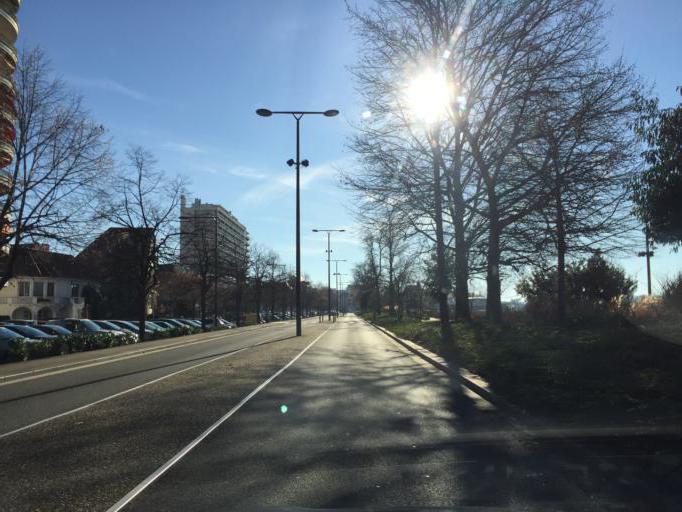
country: FR
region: Auvergne
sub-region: Departement de l'Allier
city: Vichy
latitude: 46.1323
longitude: 3.4151
